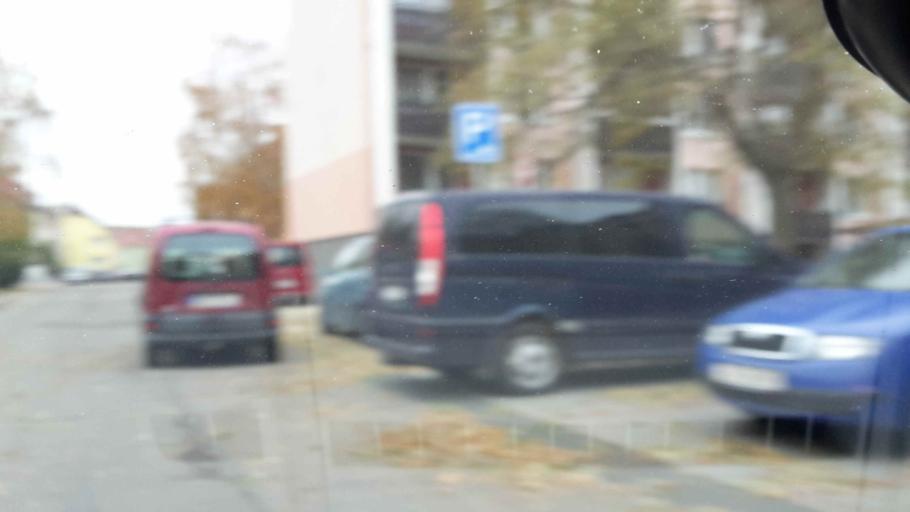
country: CZ
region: South Moravian
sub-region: Mesto Brno
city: Mokra Hora
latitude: 49.2305
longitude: 16.5872
